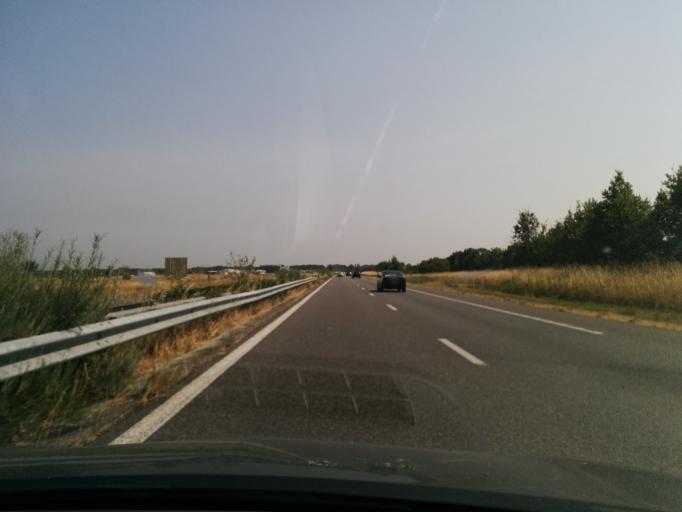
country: FR
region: Midi-Pyrenees
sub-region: Departement du Tarn
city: Coufouleux
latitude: 43.7849
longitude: 1.7383
